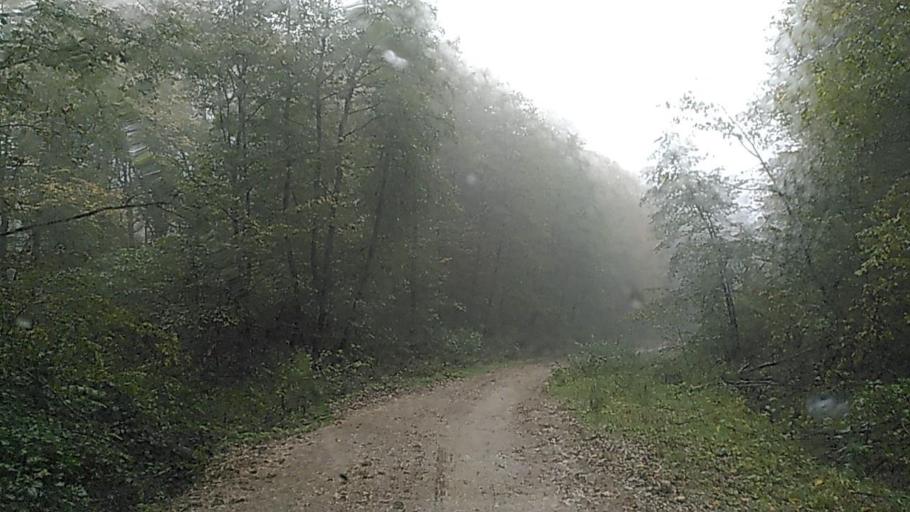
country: RU
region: Kabardino-Balkariya
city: Belaya Rechka
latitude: 43.3624
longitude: 43.4154
